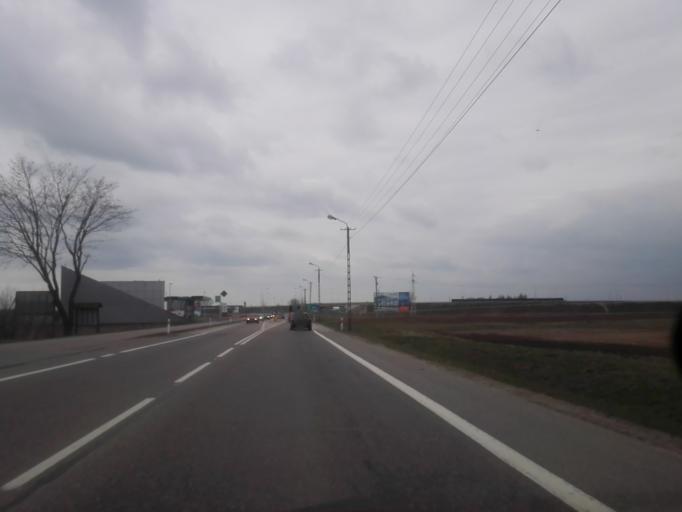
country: PL
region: Podlasie
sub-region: Powiat augustowski
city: Augustow
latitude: 53.8339
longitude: 22.9654
